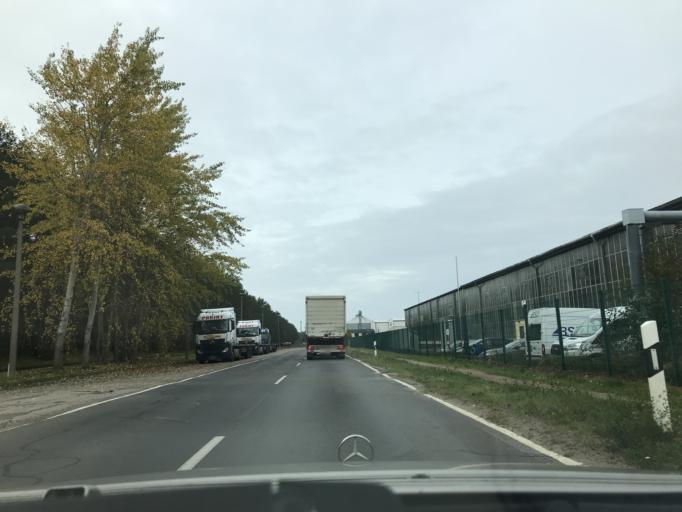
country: DE
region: Mecklenburg-Vorpommern
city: Lubmin
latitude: 54.1374
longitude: 13.6656
